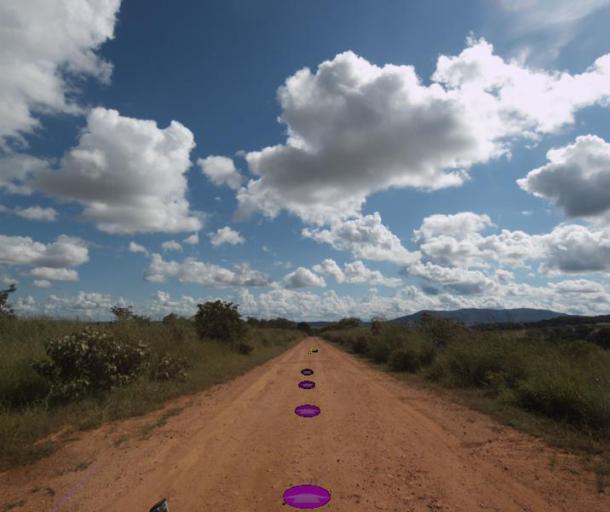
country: BR
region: Goias
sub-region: Jaragua
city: Jaragua
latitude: -15.8200
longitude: -49.2194
